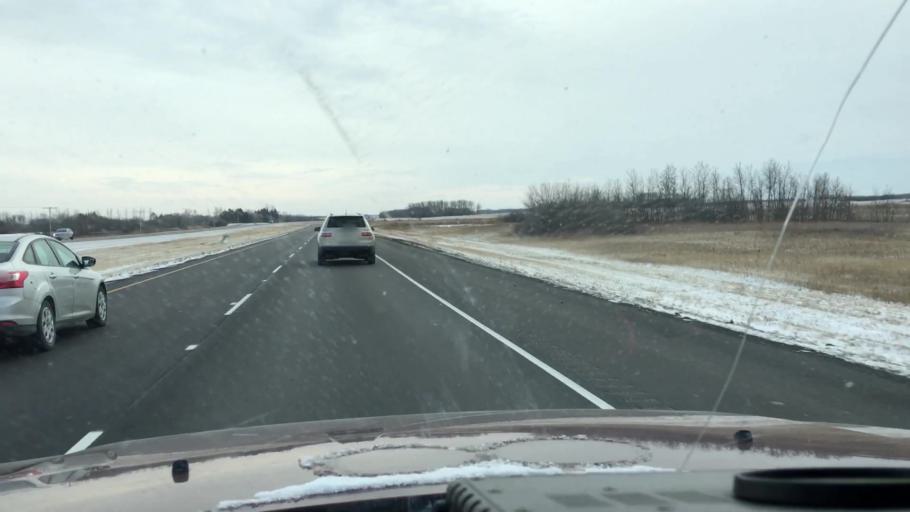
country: CA
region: Saskatchewan
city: Saskatoon
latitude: 52.0214
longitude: -106.5787
